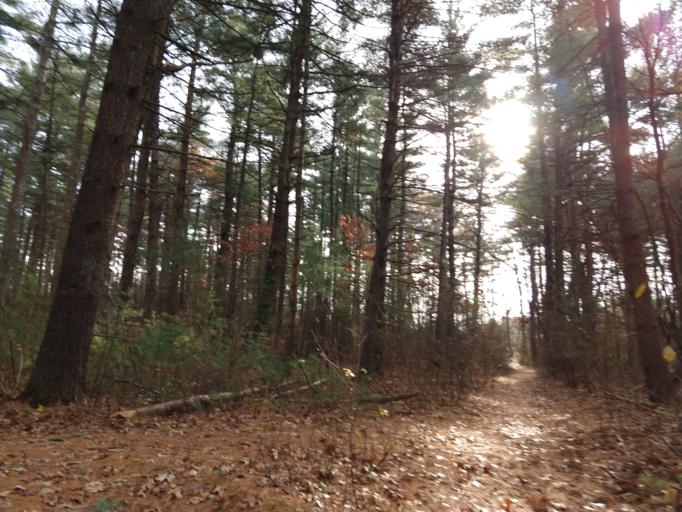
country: US
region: Massachusetts
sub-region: Middlesex County
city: Billerica
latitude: 42.5817
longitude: -71.3019
